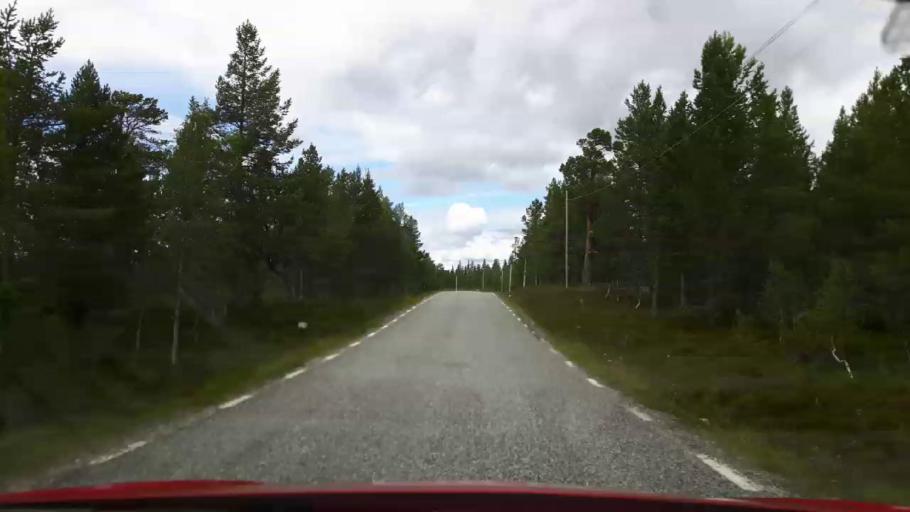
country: NO
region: Hedmark
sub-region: Engerdal
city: Engerdal
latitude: 62.3300
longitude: 12.8075
